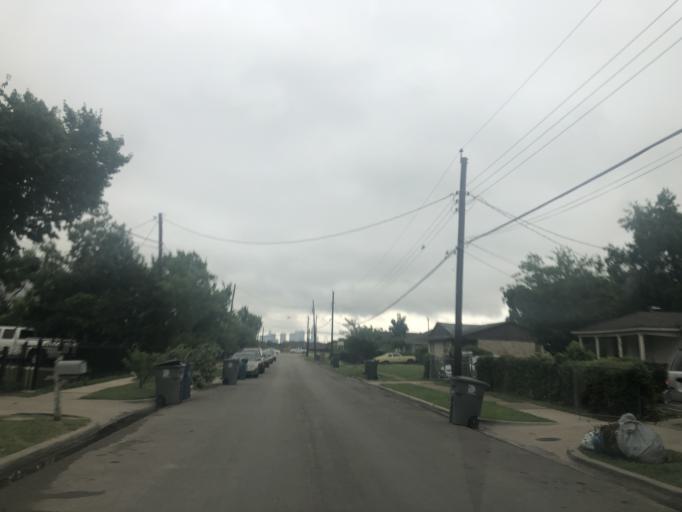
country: US
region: Texas
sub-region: Dallas County
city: Cockrell Hill
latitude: 32.7838
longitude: -96.8758
